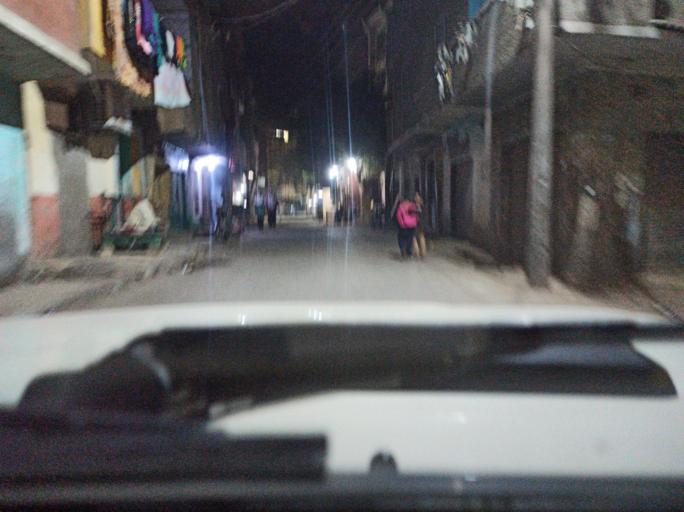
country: EG
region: Muhafazat Bani Suwayf
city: Bani Suwayf
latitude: 29.0770
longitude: 31.0874
